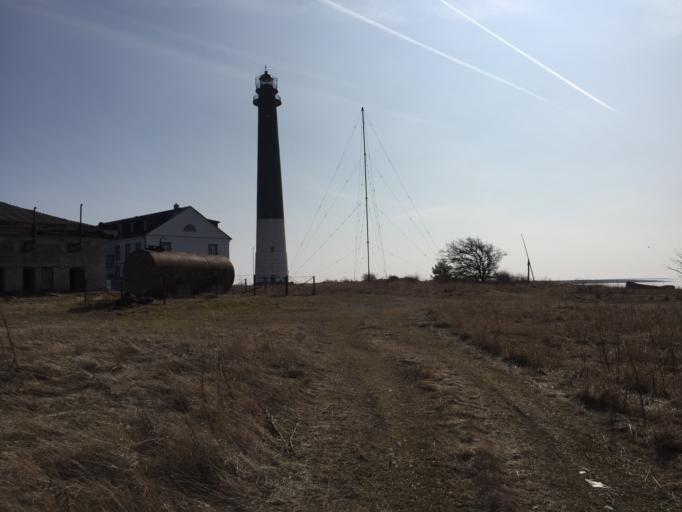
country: LV
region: Dundaga
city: Dundaga
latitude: 57.9111
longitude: 22.0548
